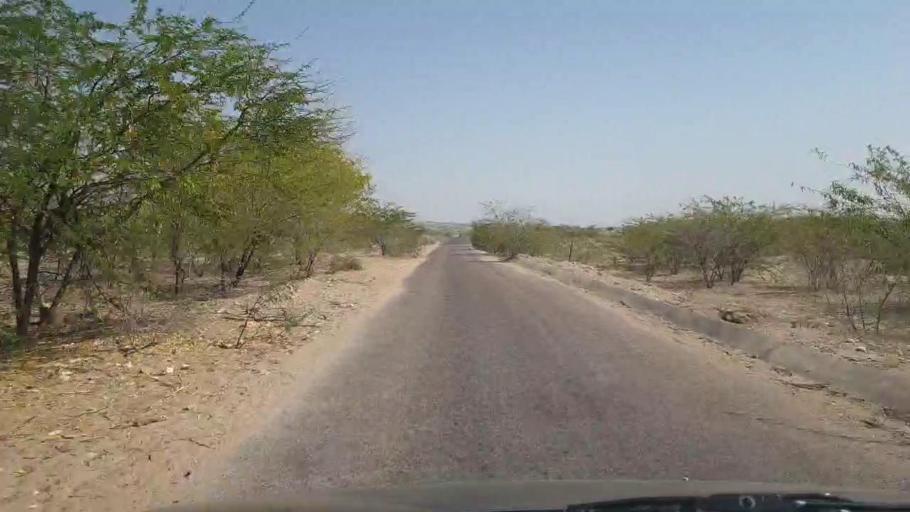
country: PK
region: Sindh
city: Chor
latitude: 25.5665
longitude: 69.8971
